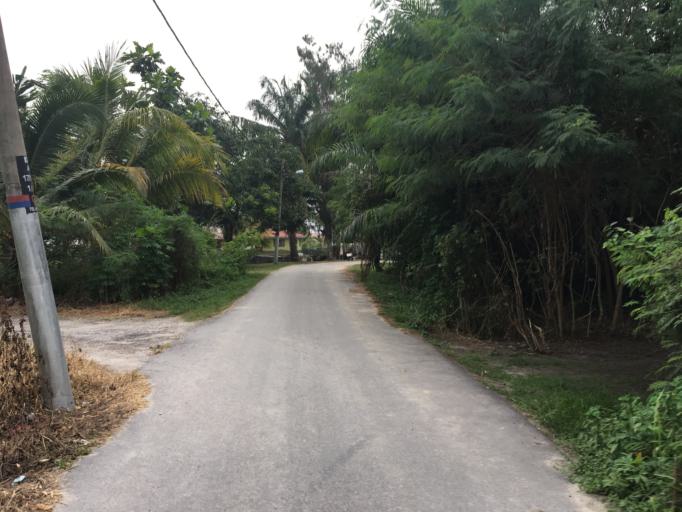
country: MY
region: Perak
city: Lumut
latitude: 4.2983
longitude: 100.6705
